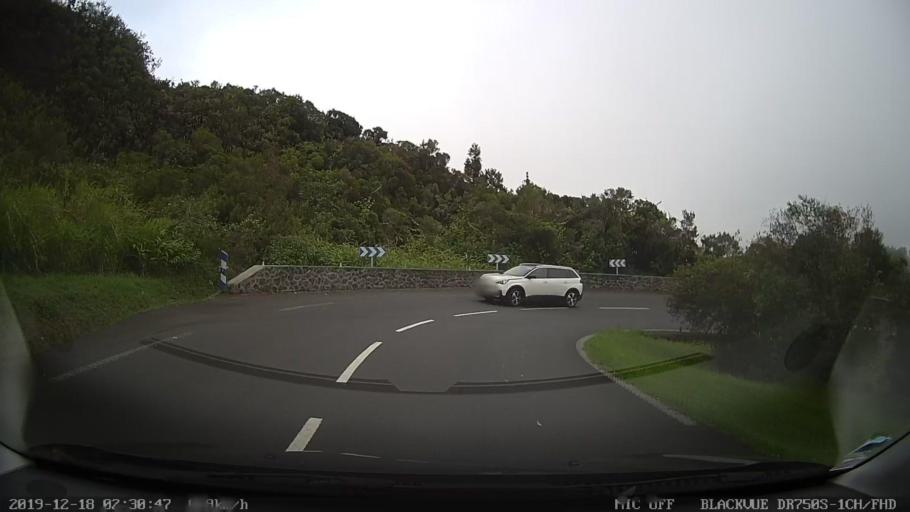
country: RE
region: Reunion
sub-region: Reunion
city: Cilaos
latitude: -21.1544
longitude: 55.6030
